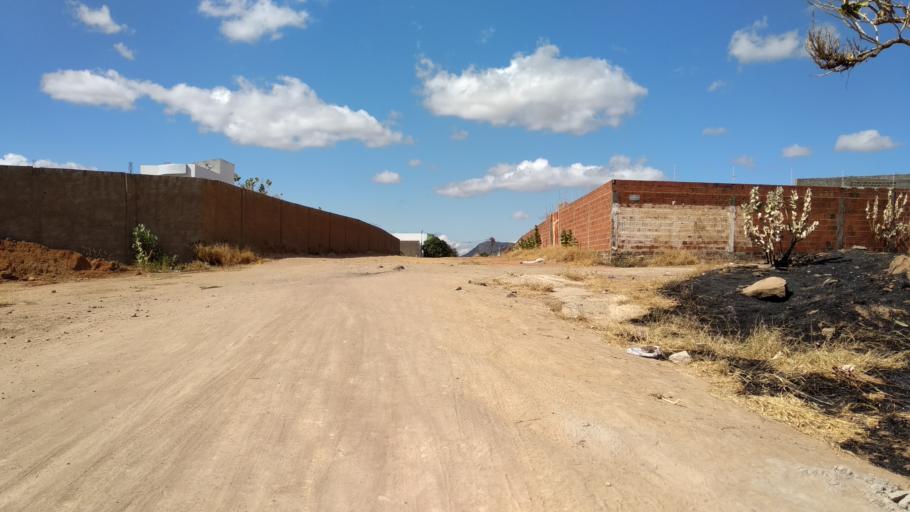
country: BR
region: Bahia
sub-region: Guanambi
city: Guanambi
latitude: -14.2299
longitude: -42.7784
